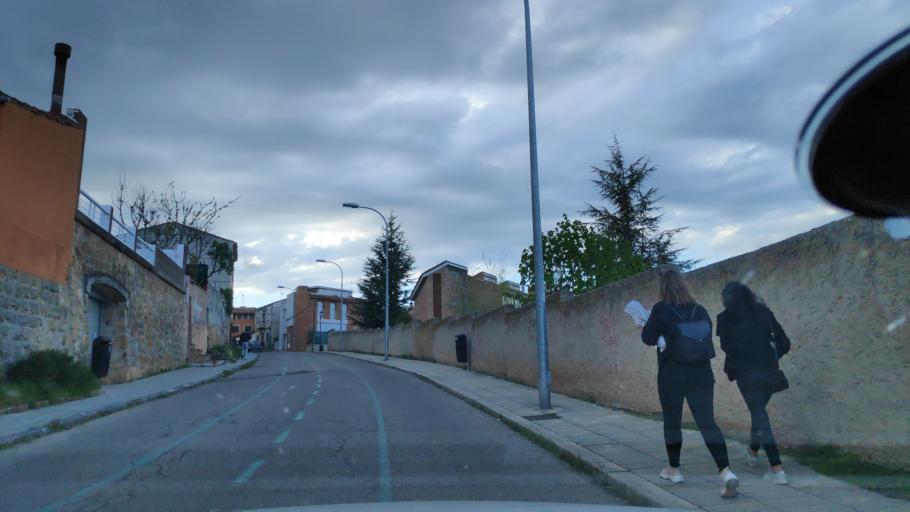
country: ES
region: Castille and Leon
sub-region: Provincia de Soria
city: Soria
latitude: 41.7649
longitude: -2.4564
